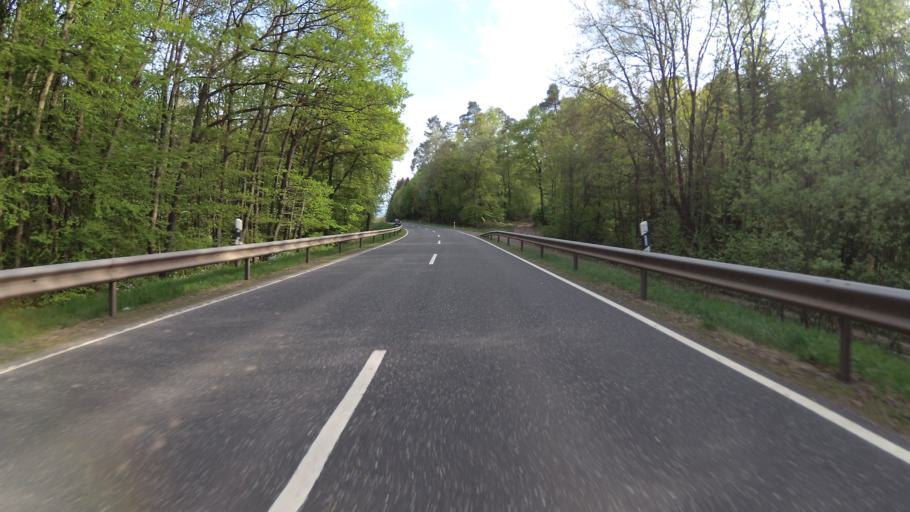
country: DE
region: Rheinland-Pfalz
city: Bausendorf
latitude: 50.0262
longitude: 6.9979
